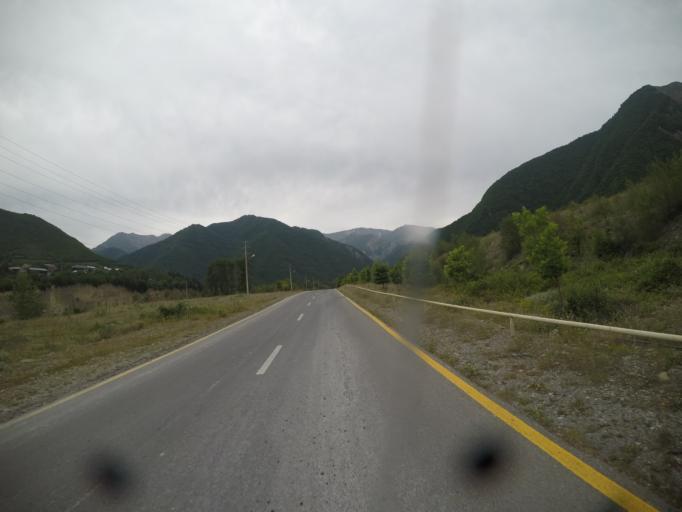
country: AZ
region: Shaki City
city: Sheki
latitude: 41.2499
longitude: 47.2039
